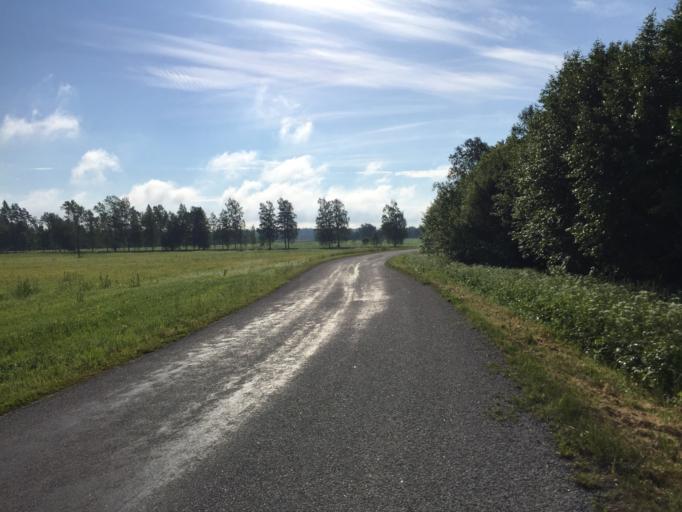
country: EE
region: Jogevamaa
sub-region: Mustvee linn
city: Mustvee
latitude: 59.0003
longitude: 26.9416
